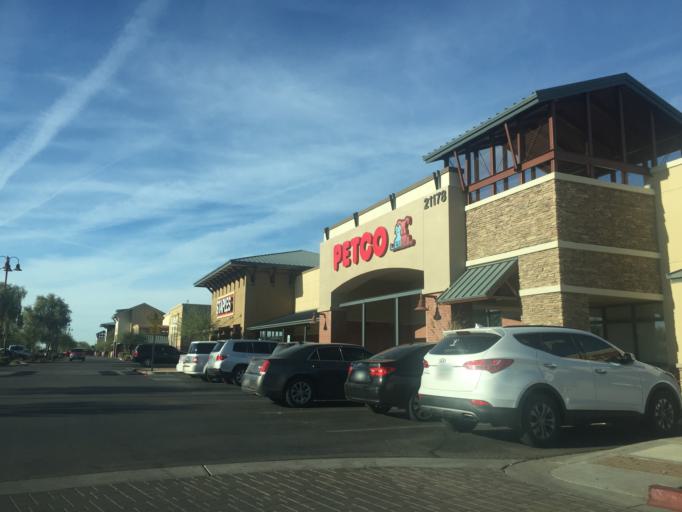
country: US
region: Arizona
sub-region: Maricopa County
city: Queen Creek
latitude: 33.2499
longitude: -111.6283
